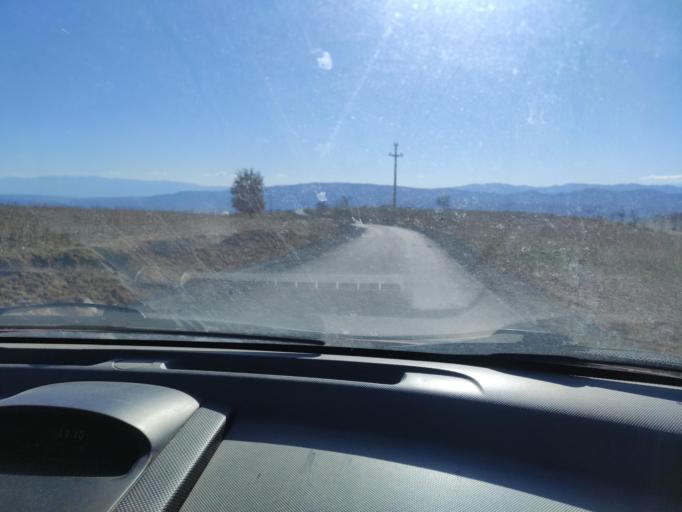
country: MK
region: Radovis
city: Radovish
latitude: 41.6632
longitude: 22.4093
